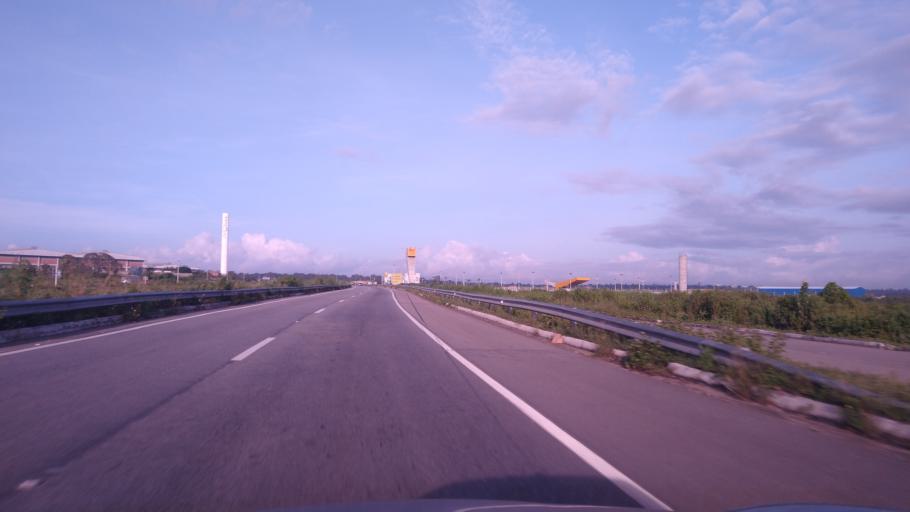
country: BR
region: Ceara
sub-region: Pacajus
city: Pacajus
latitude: -4.1622
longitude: -38.4857
